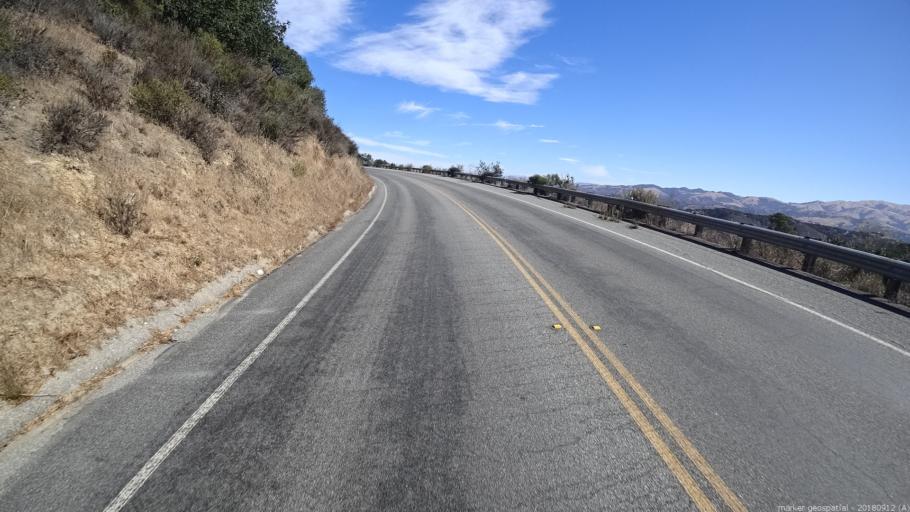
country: US
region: California
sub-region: Monterey County
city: Carmel Valley Village
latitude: 36.5309
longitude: -121.7494
